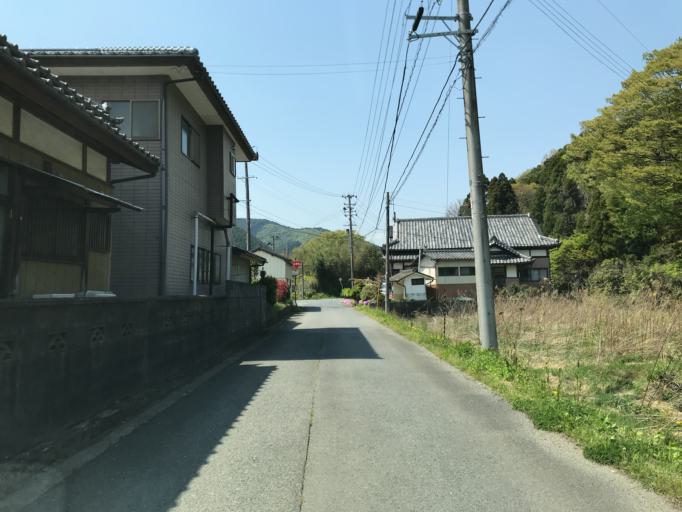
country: JP
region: Ibaraki
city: Kitaibaraki
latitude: 36.9284
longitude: 140.7410
